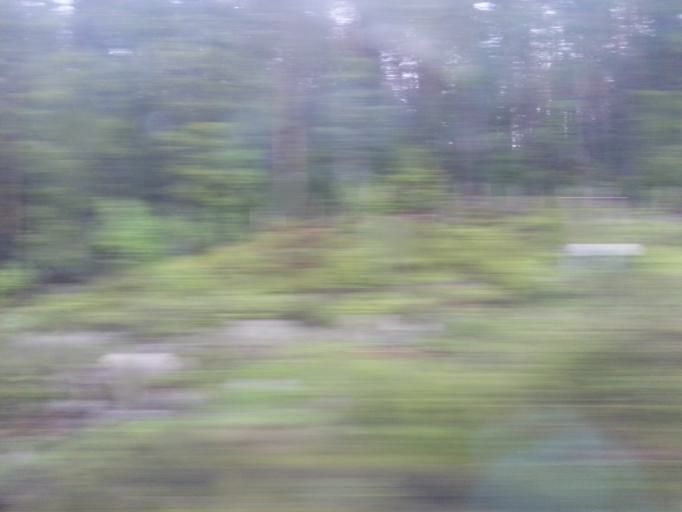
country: NO
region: Sor-Trondelag
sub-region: Rennebu
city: Berkak
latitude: 62.7058
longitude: 9.9600
